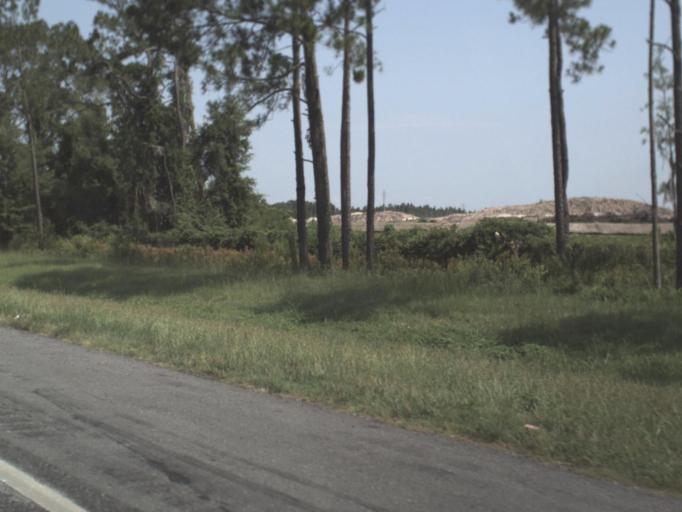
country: US
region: Florida
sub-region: Hamilton County
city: Jasper
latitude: 30.4529
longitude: -82.9396
